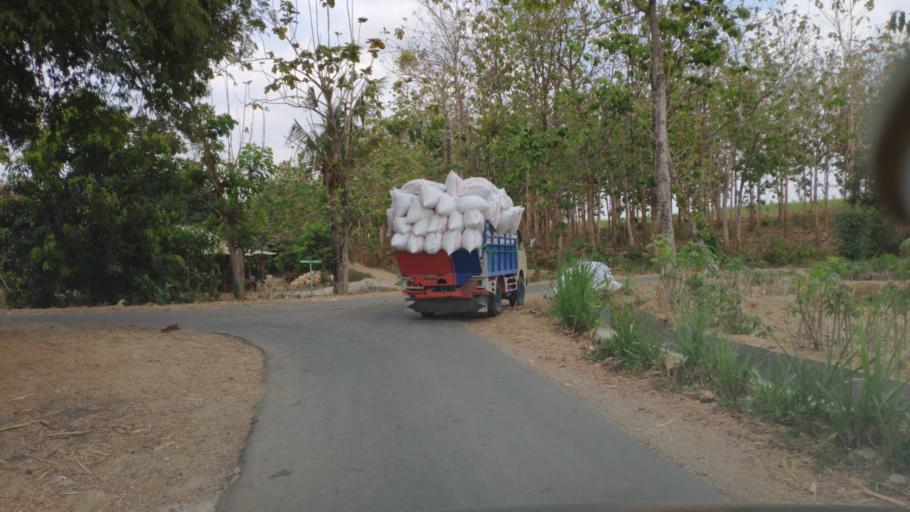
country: ID
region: Central Java
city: Kedungbacin
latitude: -6.8708
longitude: 111.2237
